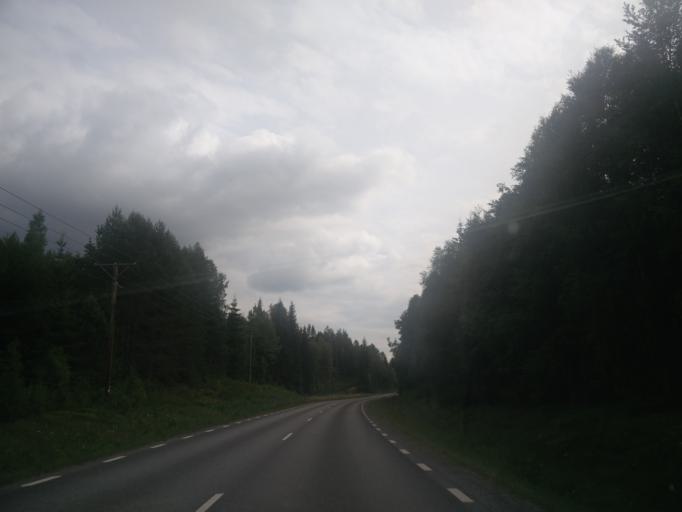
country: SE
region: Vaermland
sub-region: Arvika Kommun
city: Arvika
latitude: 59.7227
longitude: 12.5679
